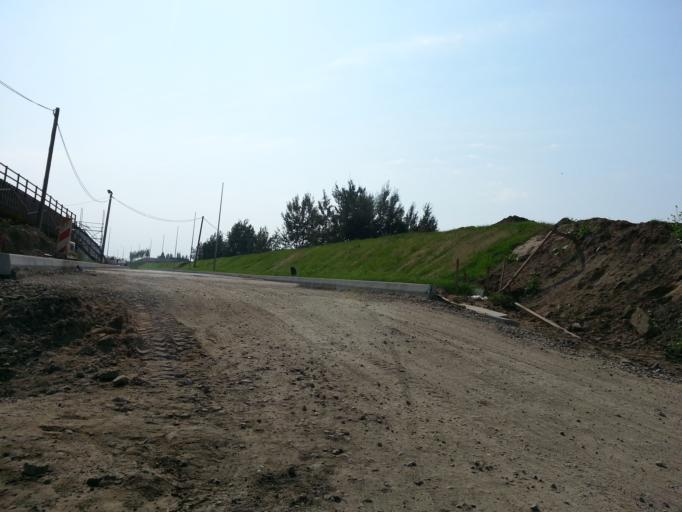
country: LT
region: Vilnius County
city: Pasilaiciai
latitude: 54.7354
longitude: 25.2077
